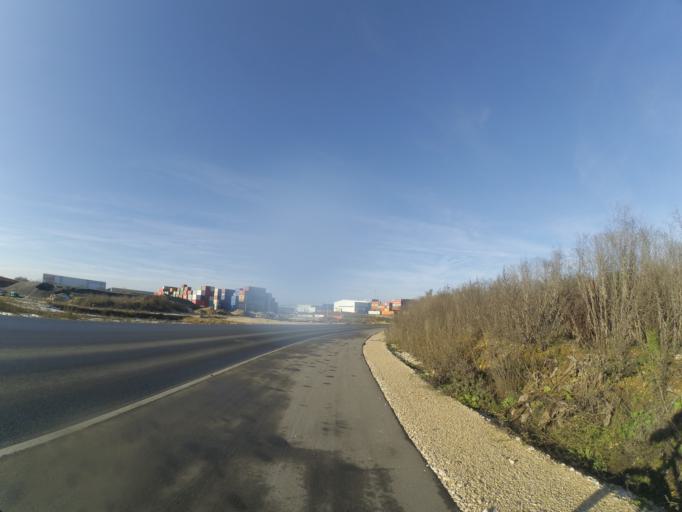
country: DE
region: Baden-Wuerttemberg
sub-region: Tuebingen Region
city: Beimerstetten
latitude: 48.4575
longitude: 9.9730
